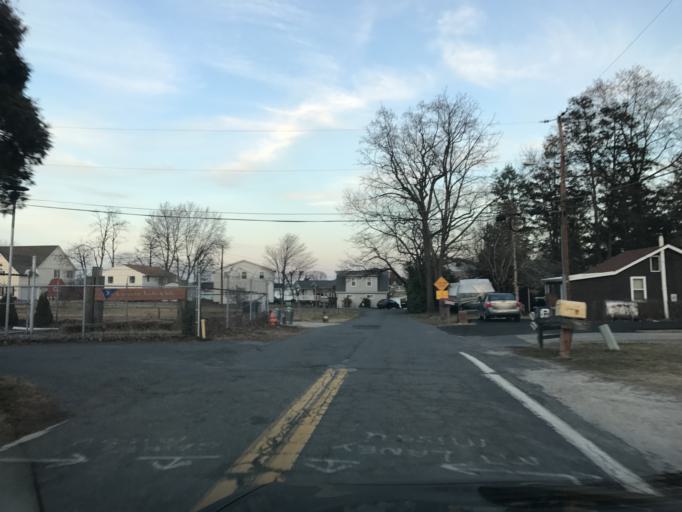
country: US
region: Maryland
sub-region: Baltimore County
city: Middle River
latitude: 39.3024
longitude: -76.4175
